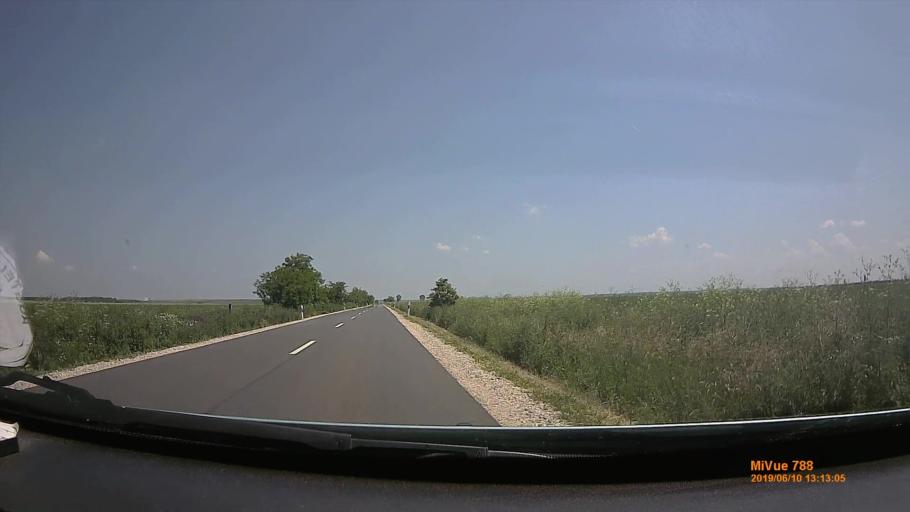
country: HU
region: Borsod-Abauj-Zemplen
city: Hernadnemeti
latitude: 48.0612
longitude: 20.9988
